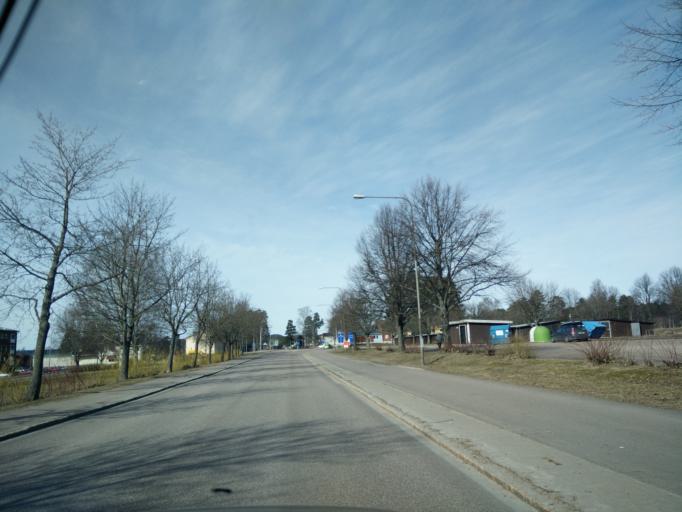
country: SE
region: Vaermland
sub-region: Hagfors Kommun
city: Hagfors
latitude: 60.0391
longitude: 13.6916
